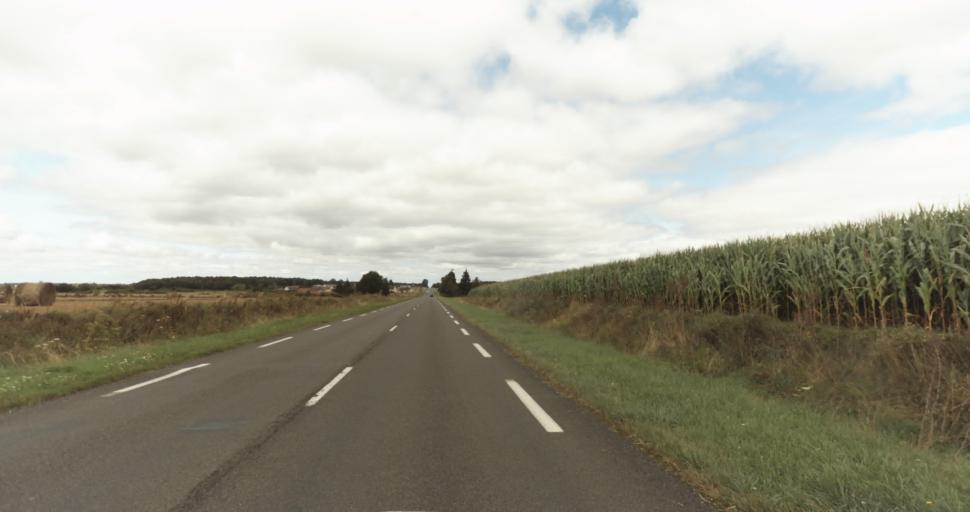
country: FR
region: Haute-Normandie
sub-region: Departement de l'Eure
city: Evreux
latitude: 48.9495
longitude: 1.1629
